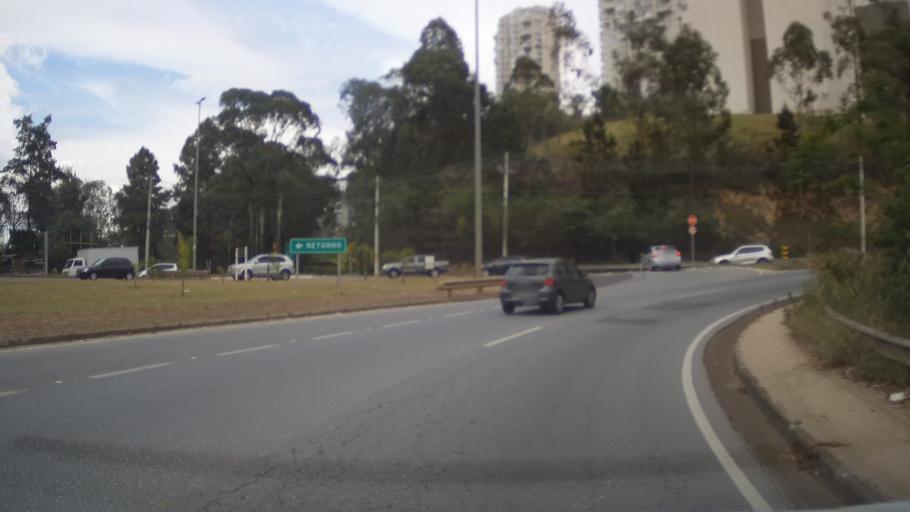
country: BR
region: Minas Gerais
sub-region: Belo Horizonte
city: Belo Horizonte
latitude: -19.9879
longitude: -43.9432
